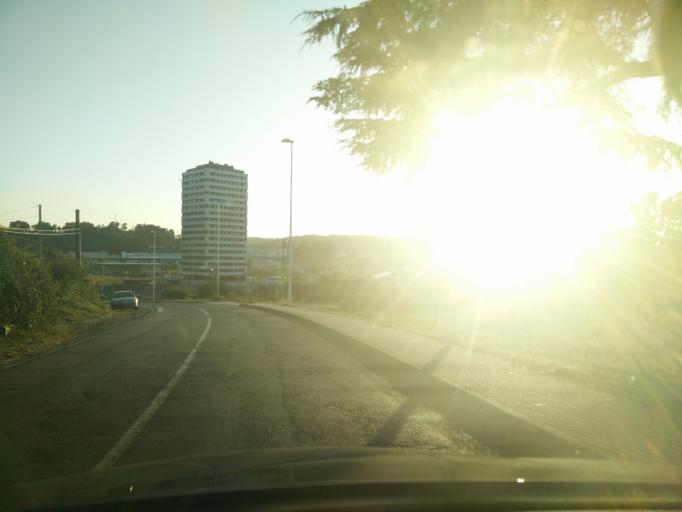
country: ES
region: Galicia
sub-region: Provincia da Coruna
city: A Coruna
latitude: 43.3357
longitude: -8.4044
